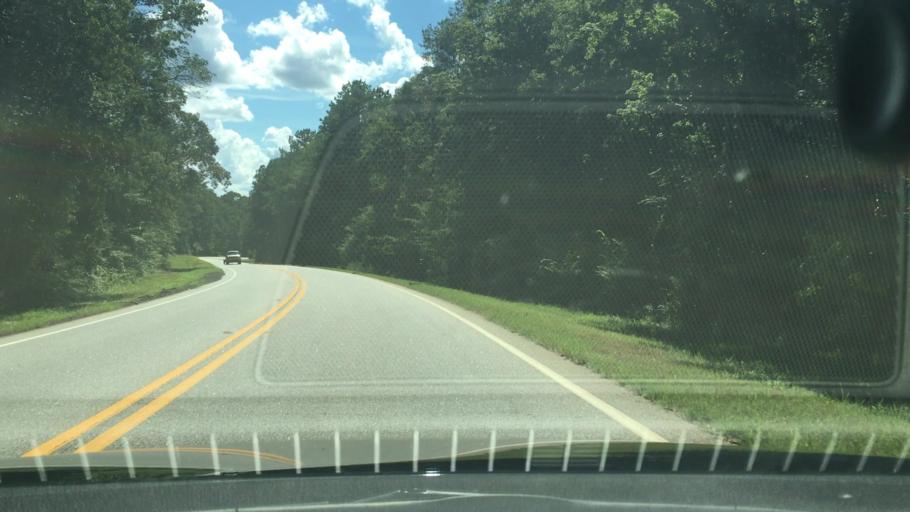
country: US
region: Georgia
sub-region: Butts County
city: Indian Springs
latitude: 33.3090
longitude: -83.8198
